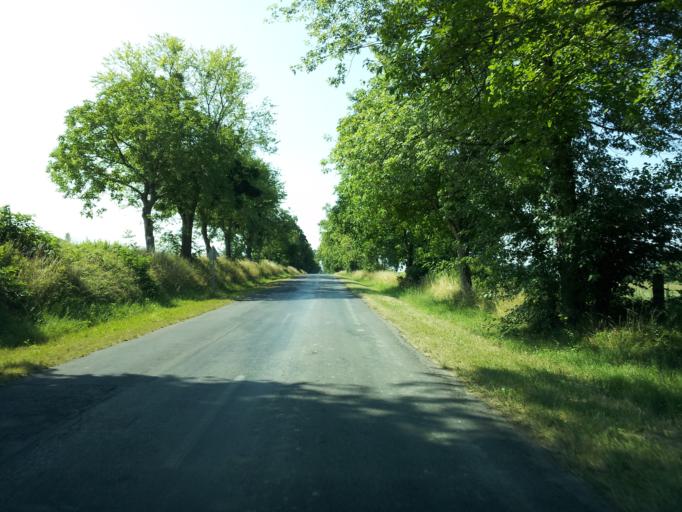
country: HU
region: Zala
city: Heviz
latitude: 46.8498
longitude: 17.1165
